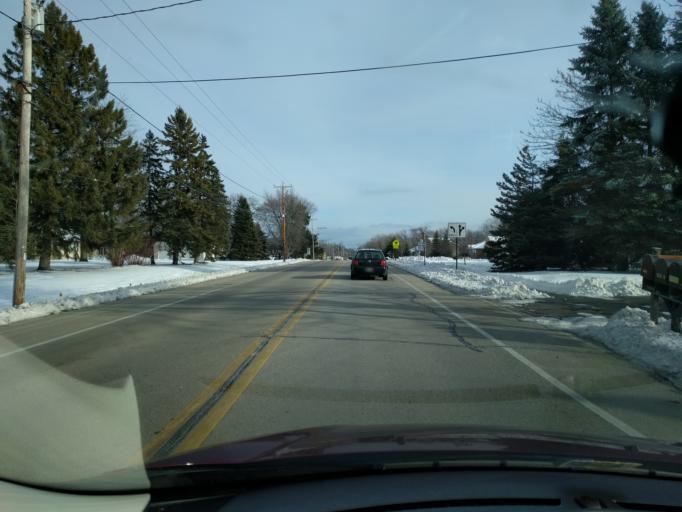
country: US
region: Wisconsin
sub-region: Milwaukee County
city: Bayside
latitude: 43.1767
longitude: -87.9075
